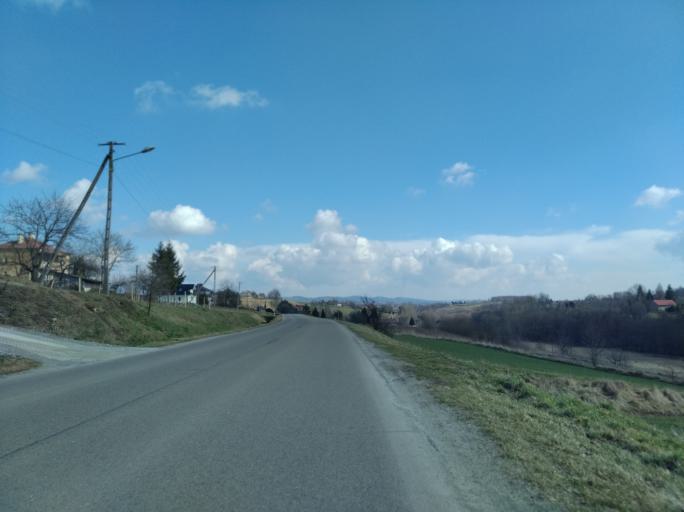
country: PL
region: Subcarpathian Voivodeship
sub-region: Powiat strzyzowski
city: Frysztak
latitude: 49.8470
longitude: 21.5528
